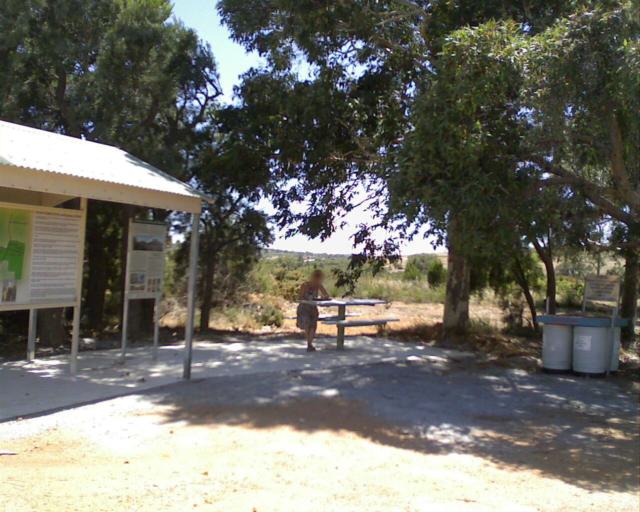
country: AU
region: Western Australia
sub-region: Dandaragan
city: Jurien Bay
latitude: -30.0573
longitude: 115.3307
